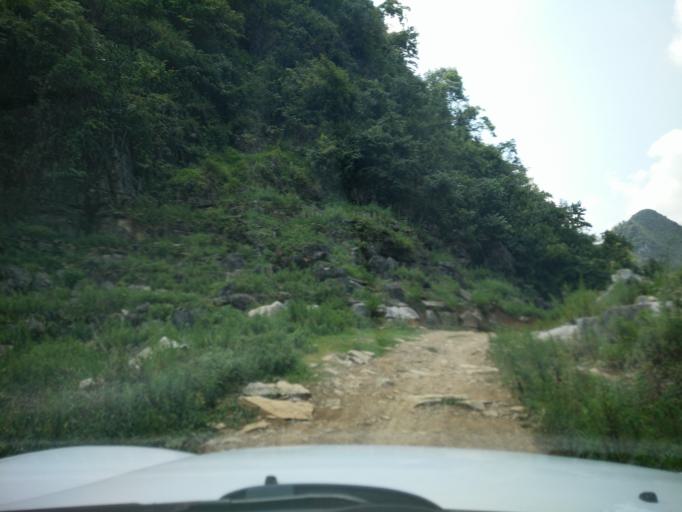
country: CN
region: Guangxi Zhuangzu Zizhiqu
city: Xinzhou
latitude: 25.0052
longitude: 105.7034
